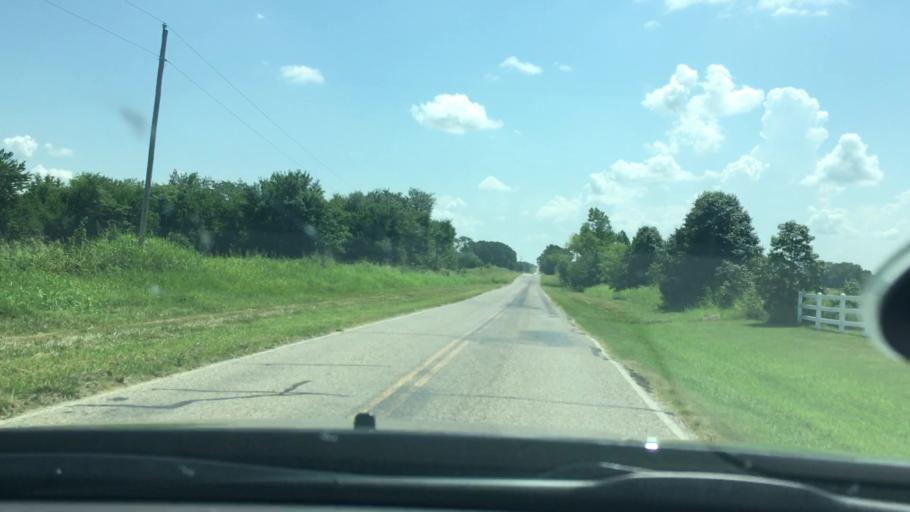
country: US
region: Oklahoma
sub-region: Pontotoc County
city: Ada
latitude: 34.6945
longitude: -96.5600
